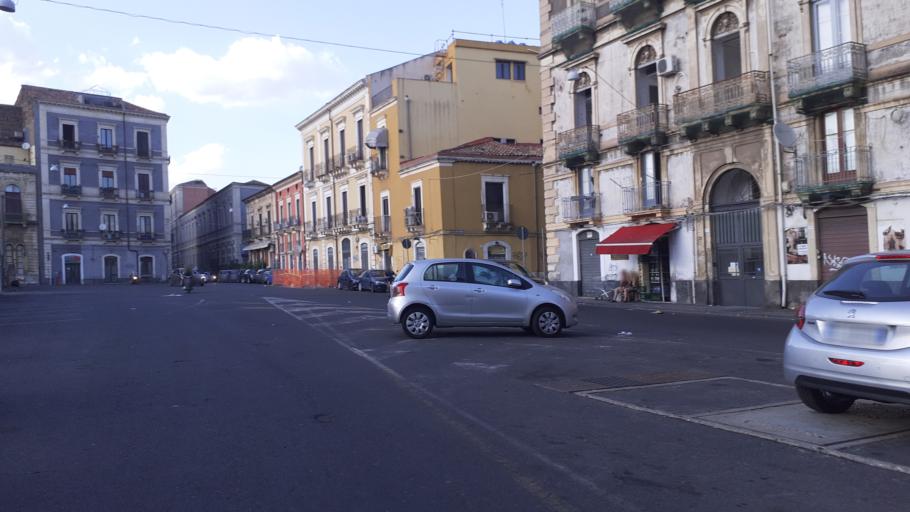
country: IT
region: Sicily
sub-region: Catania
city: Catania
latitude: 37.5086
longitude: 15.0927
